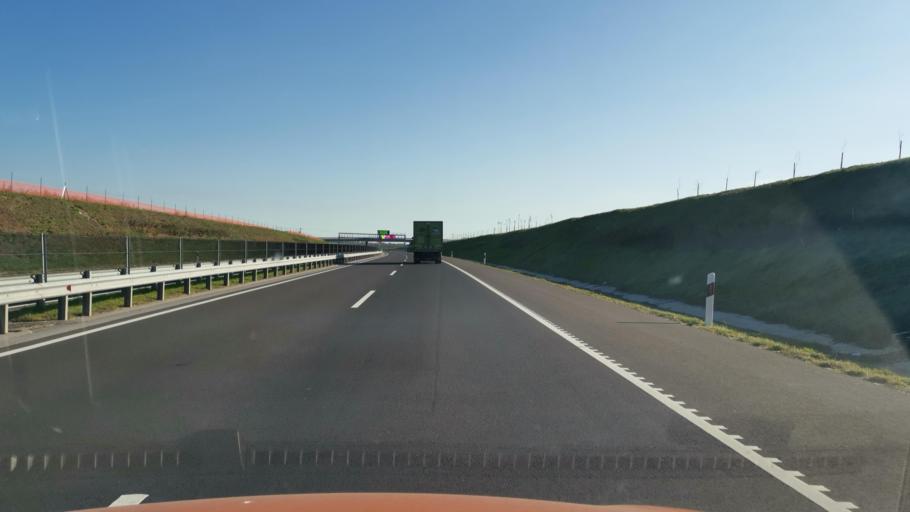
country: HU
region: Borsod-Abauj-Zemplen
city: Arnot
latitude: 48.1465
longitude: 20.8530
